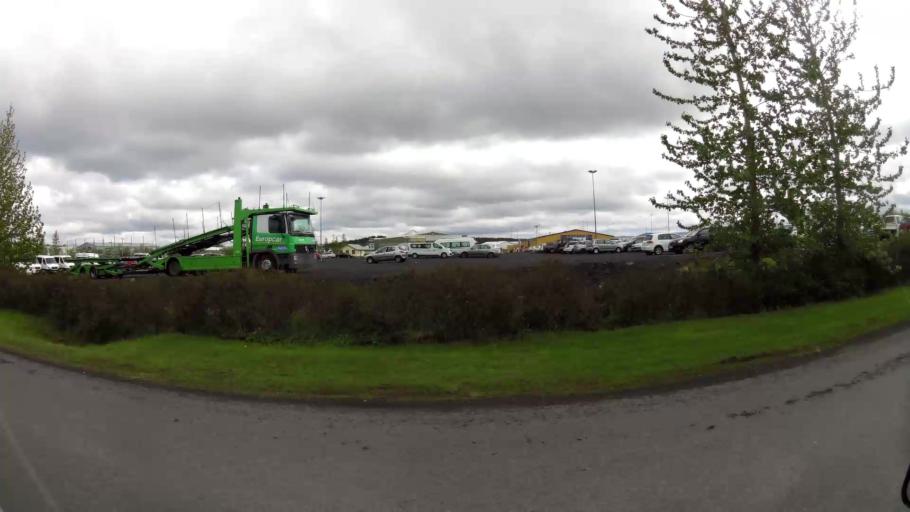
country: IS
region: Capital Region
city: Kopavogur
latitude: 64.1332
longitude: -21.9488
